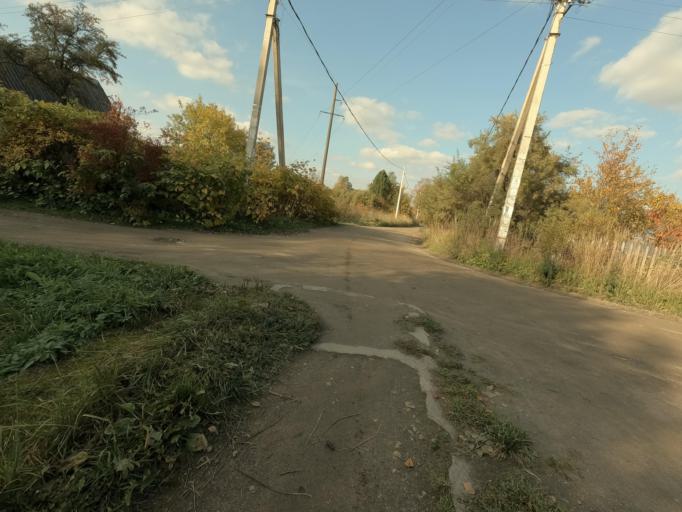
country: RU
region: Leningrad
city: Mga
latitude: 59.7628
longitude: 31.1171
